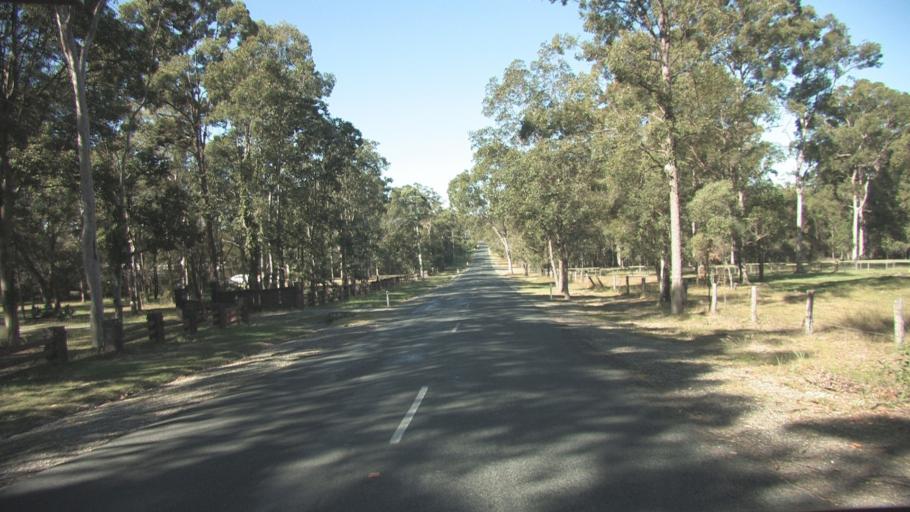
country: AU
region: Queensland
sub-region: Logan
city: Logan Reserve
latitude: -27.7306
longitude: 153.1240
